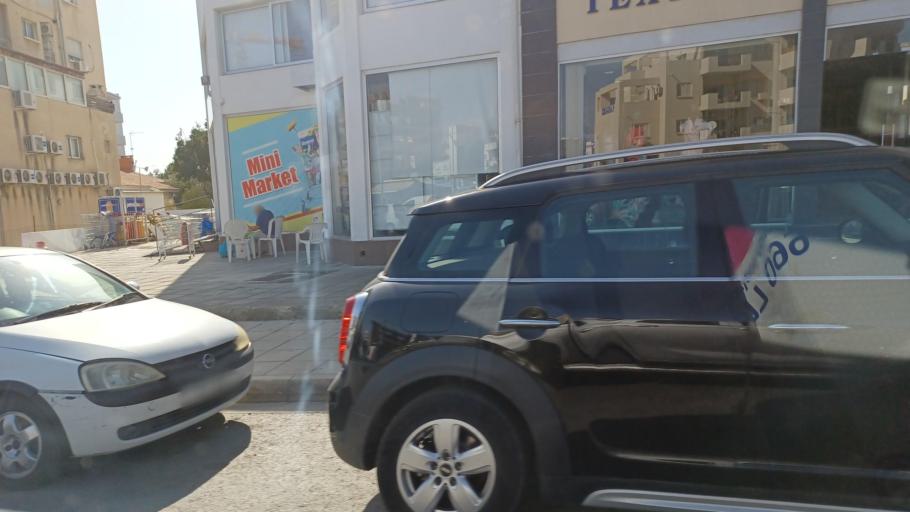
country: CY
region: Lefkosia
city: Nicosia
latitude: 35.1530
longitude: 33.3656
